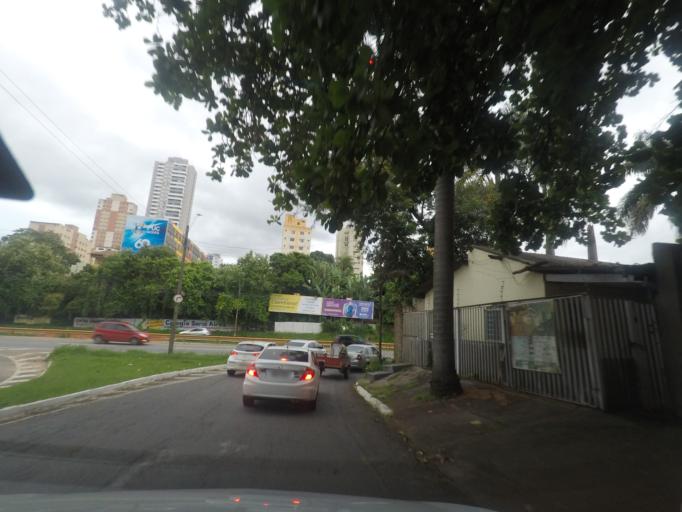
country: BR
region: Goias
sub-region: Goiania
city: Goiania
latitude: -16.6742
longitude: -49.2503
